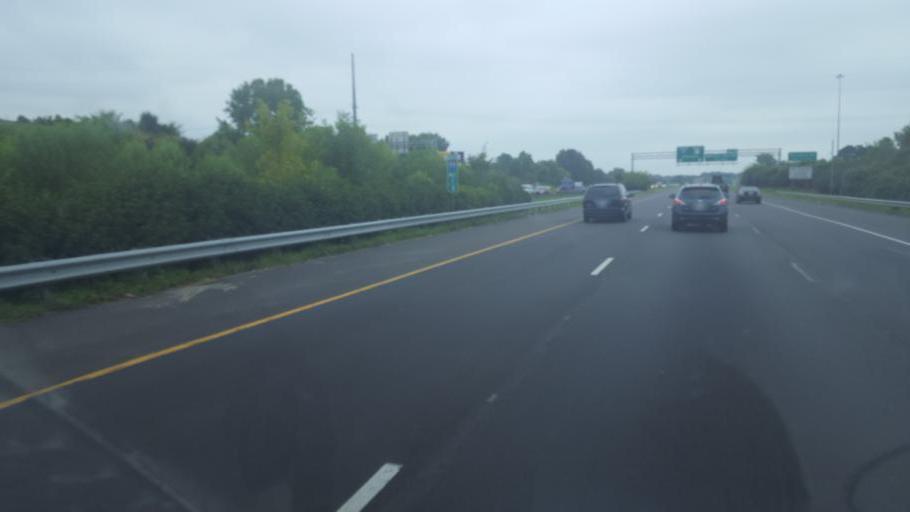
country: US
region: North Carolina
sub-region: Mecklenburg County
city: Pineville
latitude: 35.1273
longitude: -80.9161
